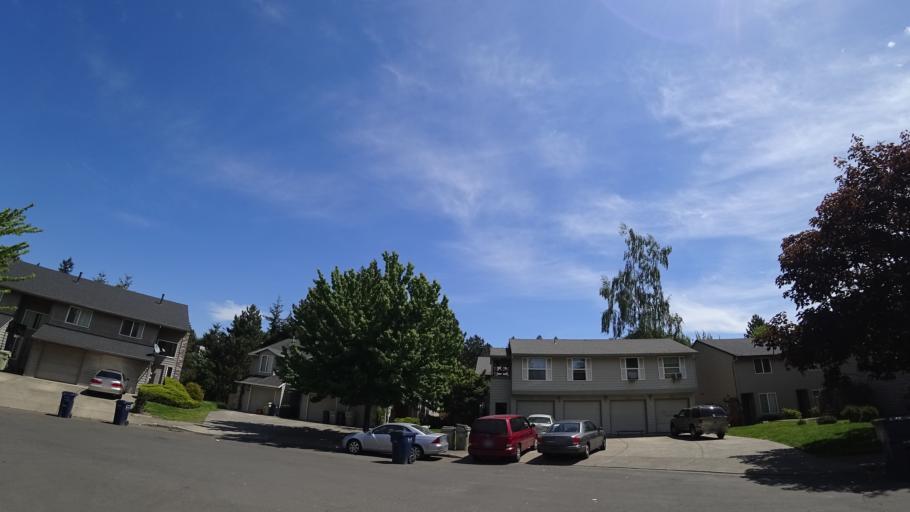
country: US
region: Oregon
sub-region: Washington County
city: Aloha
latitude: 45.4865
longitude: -122.8359
